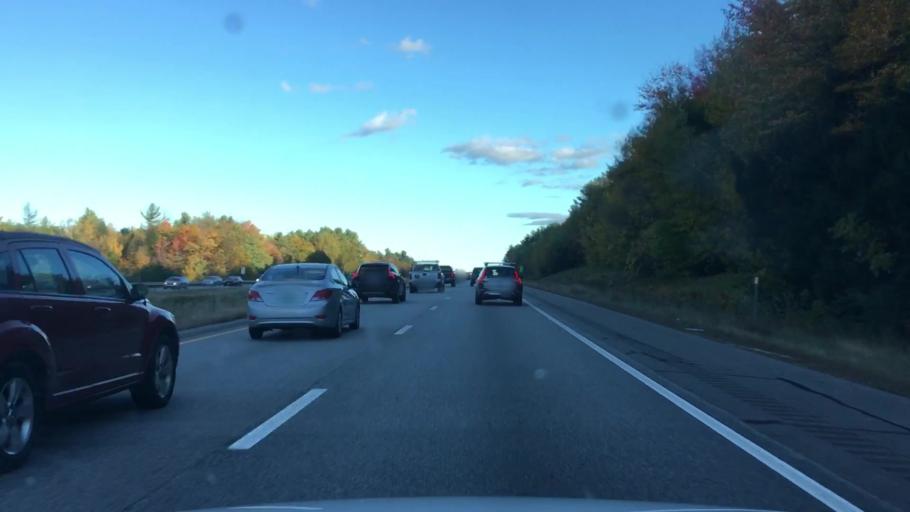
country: US
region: New Hampshire
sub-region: Rockingham County
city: Candia
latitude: 43.0282
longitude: -71.2435
